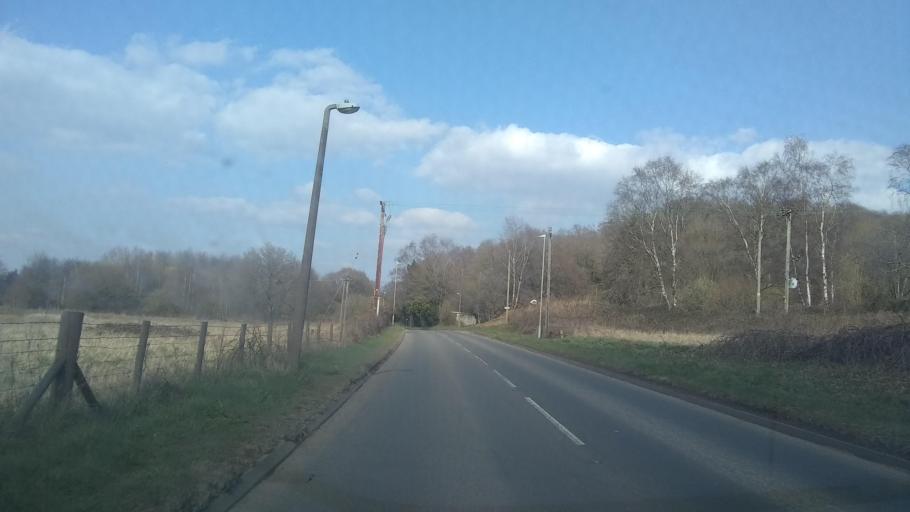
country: GB
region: England
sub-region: Worcestershire
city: Stourport-on-Severn
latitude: 52.3601
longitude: -2.2521
